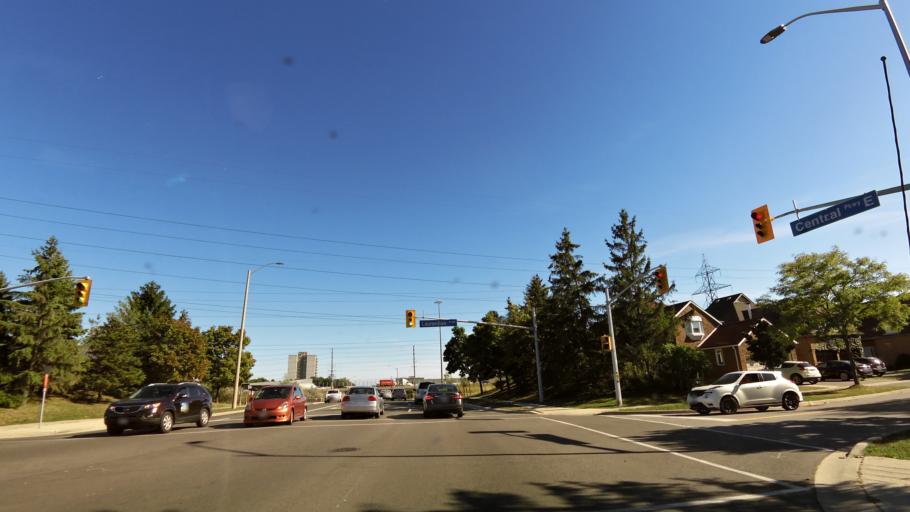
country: CA
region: Ontario
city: Mississauga
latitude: 43.6094
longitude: -79.6389
